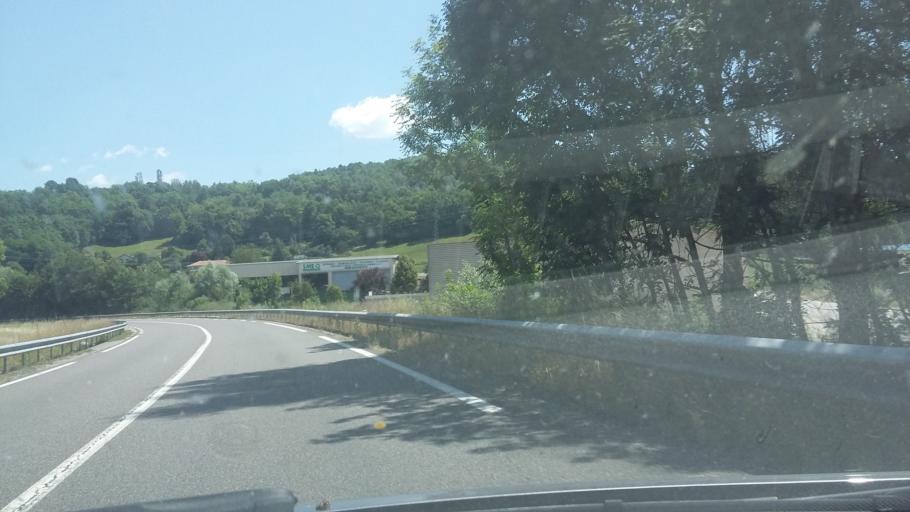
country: FR
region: Rhone-Alpes
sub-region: Departement de l'Ain
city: Belley
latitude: 45.7758
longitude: 5.6926
